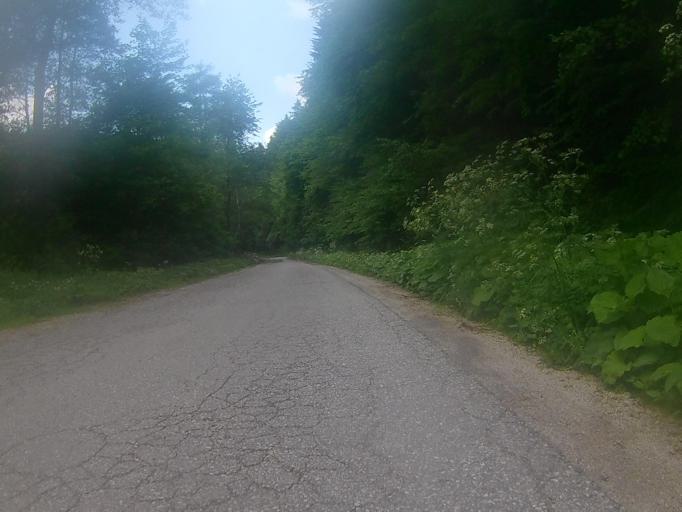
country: SI
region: Maribor
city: Bresternica
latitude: 46.6127
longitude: 15.5487
